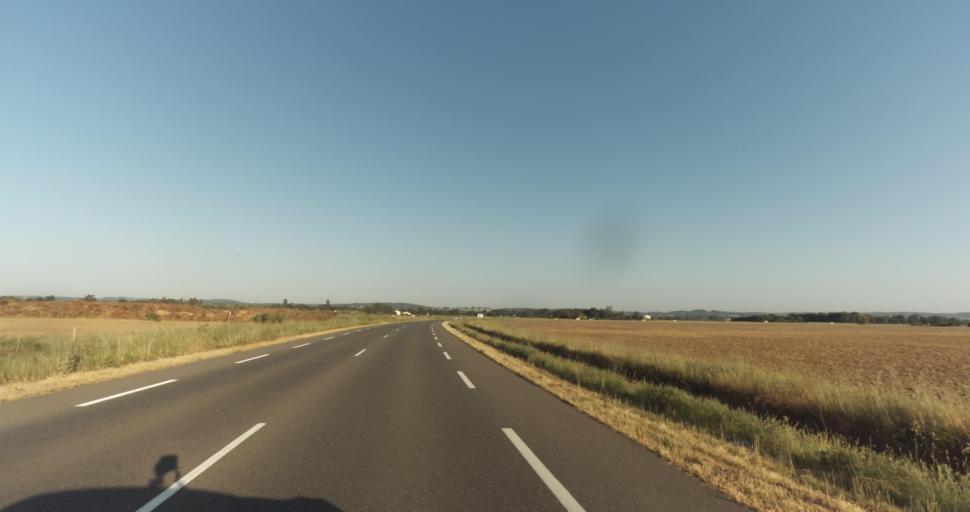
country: FR
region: Midi-Pyrenees
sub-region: Departement de la Haute-Garonne
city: Fontenilles
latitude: 43.5299
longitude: 1.1910
